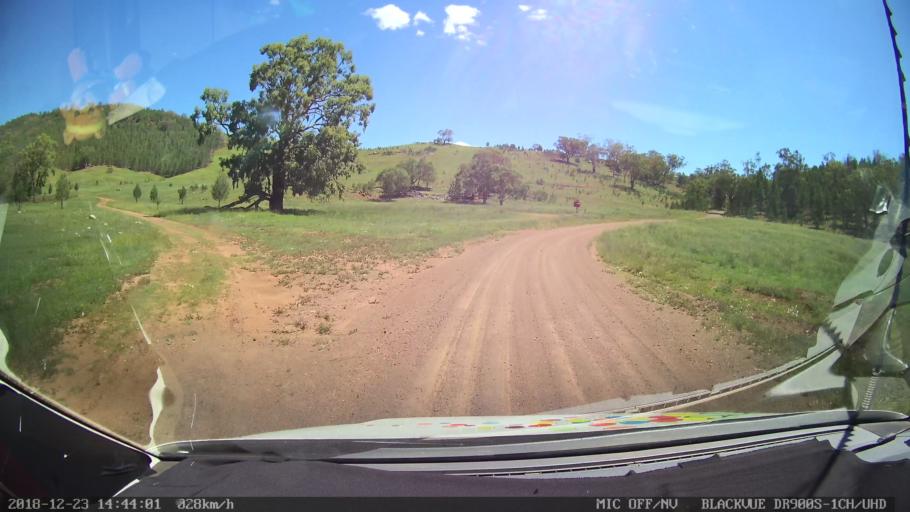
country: AU
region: New South Wales
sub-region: Tamworth Municipality
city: Manilla
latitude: -30.6450
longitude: 150.8977
